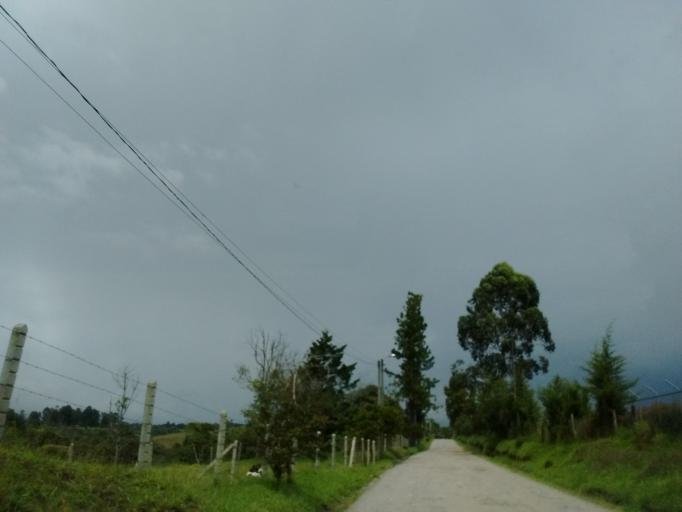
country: CO
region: Cauca
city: Cajibio
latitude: 2.5411
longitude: -76.6198
